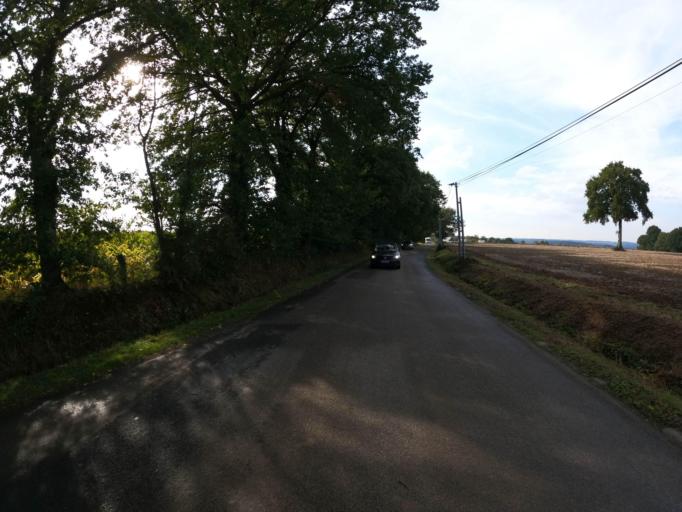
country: FR
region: Brittany
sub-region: Departement du Morbihan
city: Ploermel
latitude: 47.8709
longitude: -2.4089
